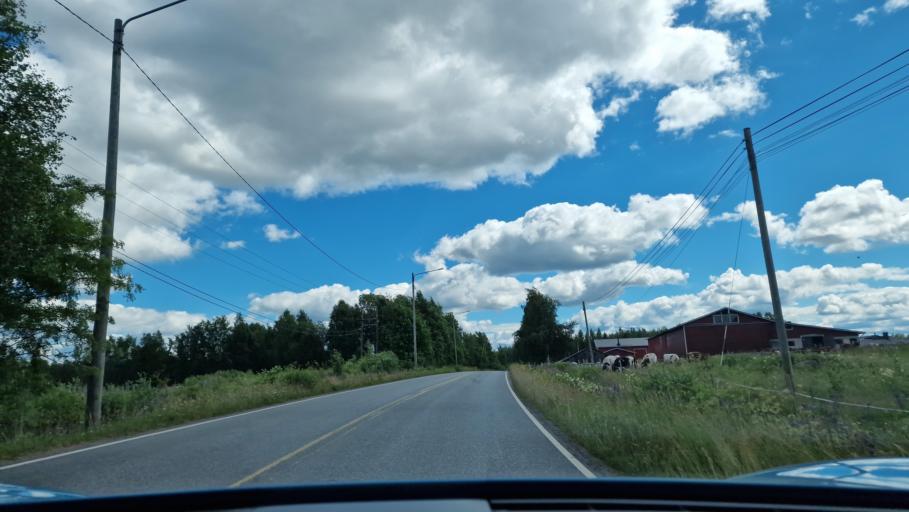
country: FI
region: Southern Ostrobothnia
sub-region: Jaerviseutu
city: Soini
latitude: 62.8438
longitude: 24.3260
